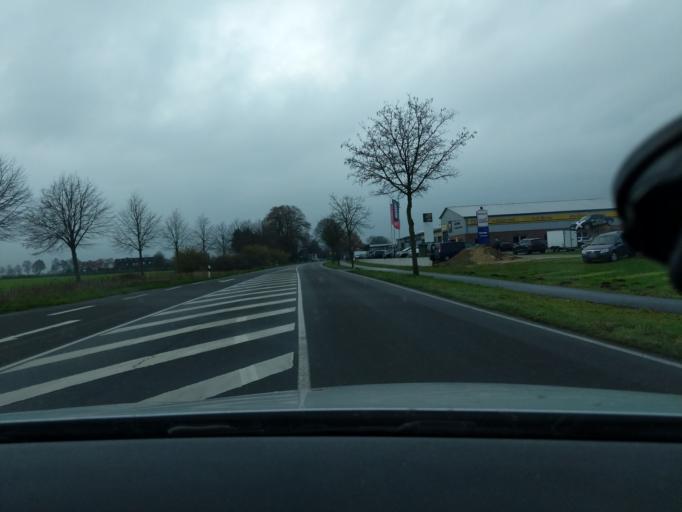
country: DE
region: Lower Saxony
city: Ahlerstedt
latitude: 53.3690
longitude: 9.4318
